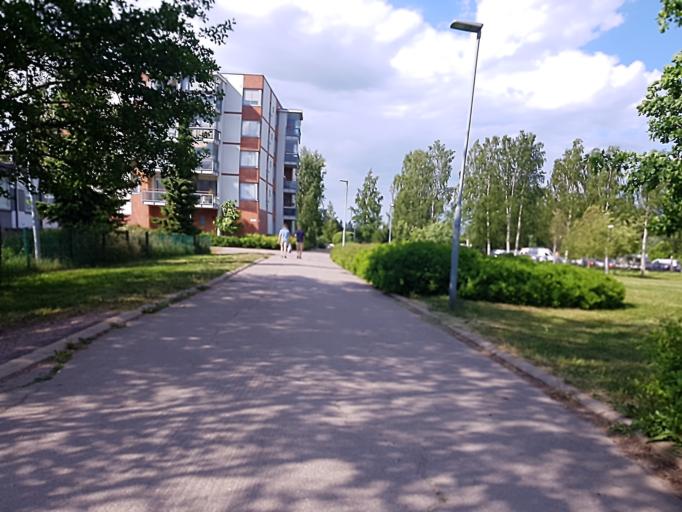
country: FI
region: Uusimaa
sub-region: Helsinki
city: Helsinki
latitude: 60.2326
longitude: 24.9817
